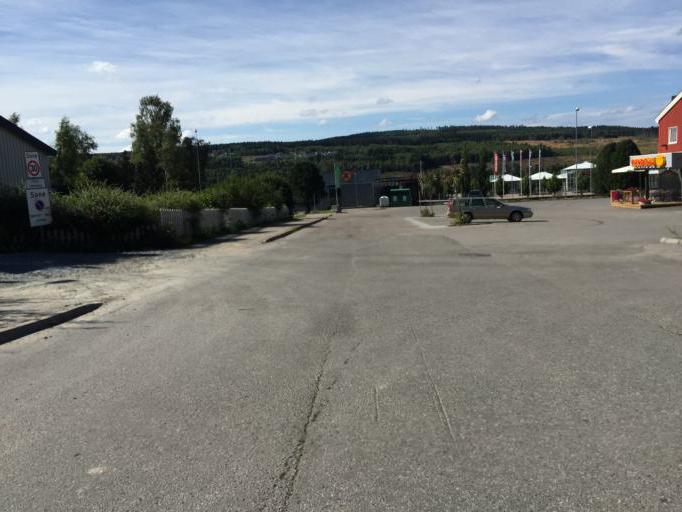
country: NO
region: Hedmark
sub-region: Kongsvinger
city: Kongsvinger
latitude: 60.2020
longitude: 11.9802
